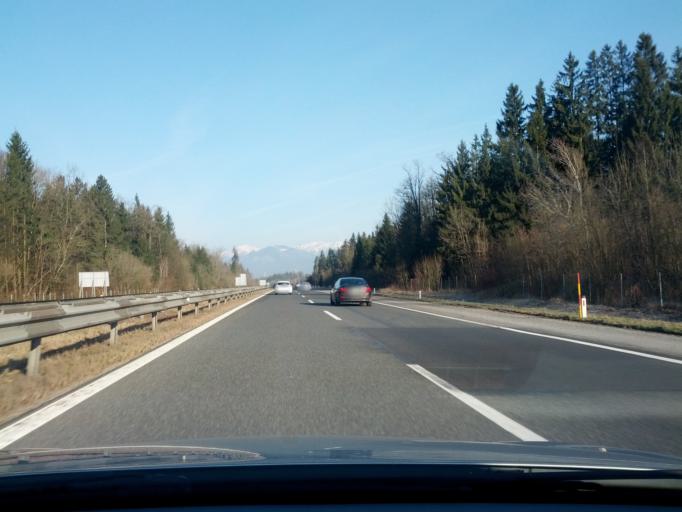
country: SI
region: Kranj
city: Britof
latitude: 46.2434
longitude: 14.3964
